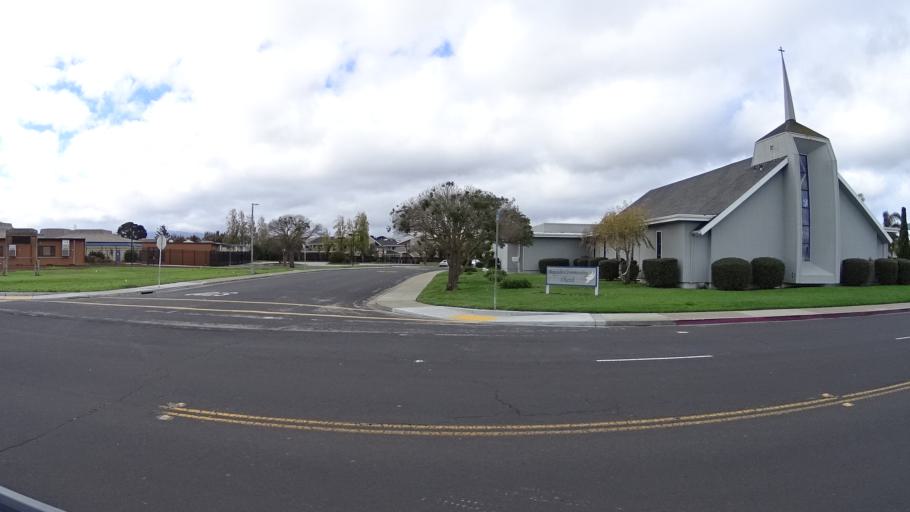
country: US
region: California
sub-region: San Mateo County
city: Foster City
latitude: 37.5609
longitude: -122.2480
